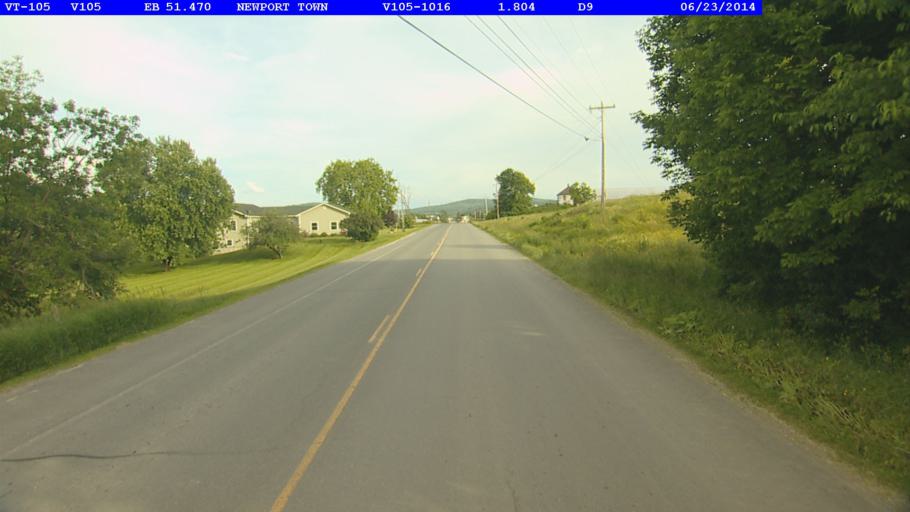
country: US
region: Vermont
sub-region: Orleans County
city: Newport
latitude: 44.9608
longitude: -72.3119
